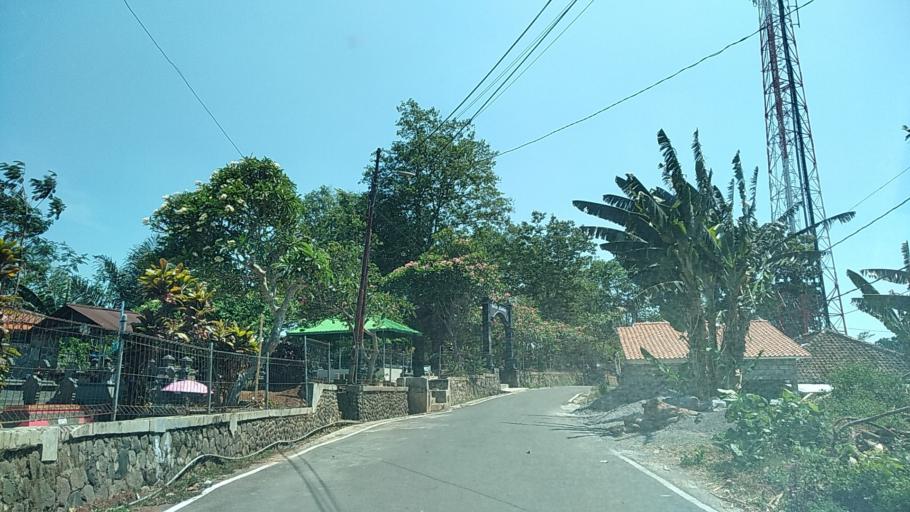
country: ID
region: Central Java
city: Ungaran
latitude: -7.1030
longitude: 110.4131
